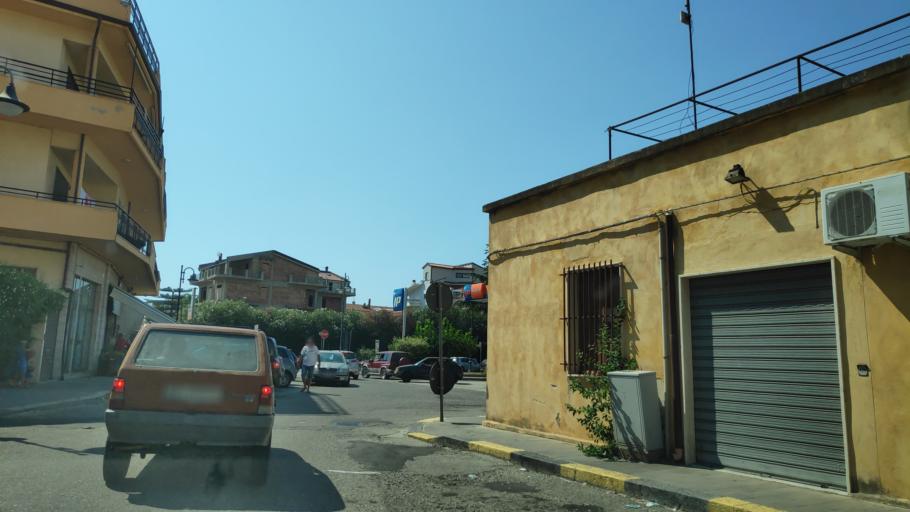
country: IT
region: Calabria
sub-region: Provincia di Reggio Calabria
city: Caulonia Marina
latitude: 38.3435
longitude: 16.4650
